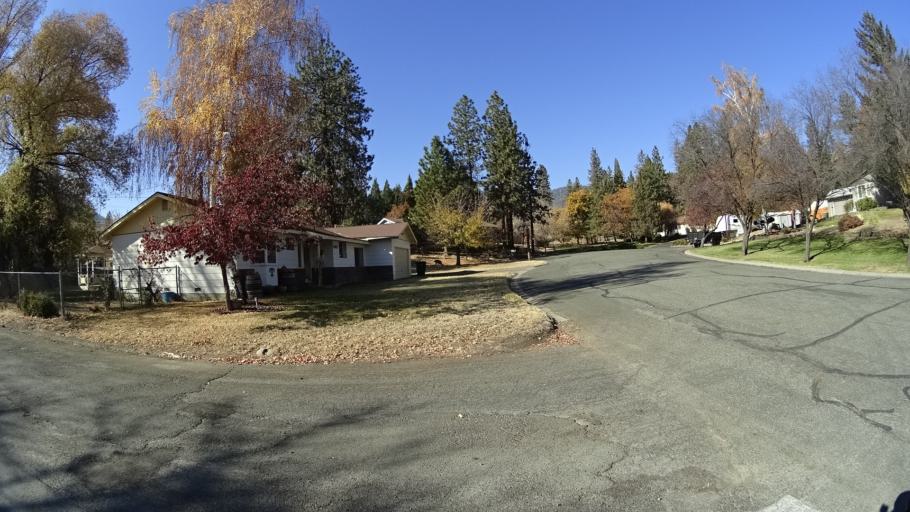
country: US
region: California
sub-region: Siskiyou County
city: Yreka
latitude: 41.7363
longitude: -122.6501
